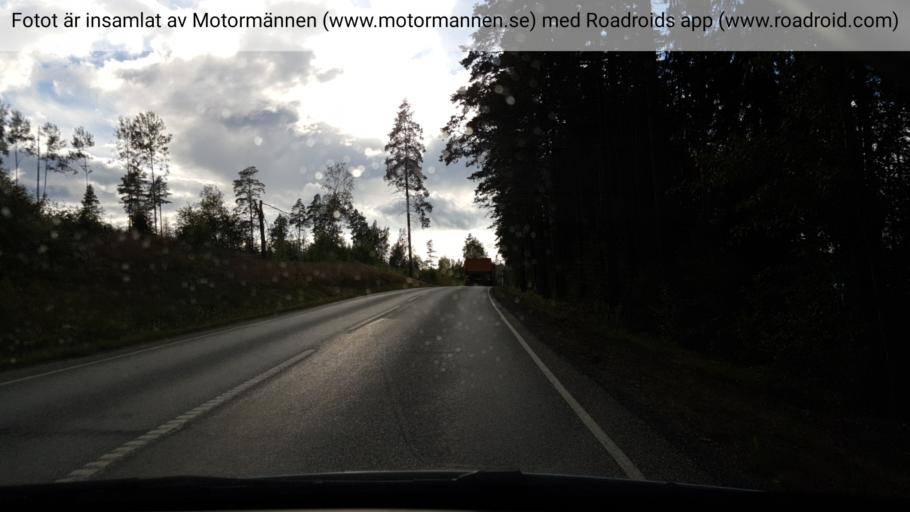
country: SE
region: OErebro
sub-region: Hallefors Kommun
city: Haellefors
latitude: 59.8027
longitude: 14.7124
